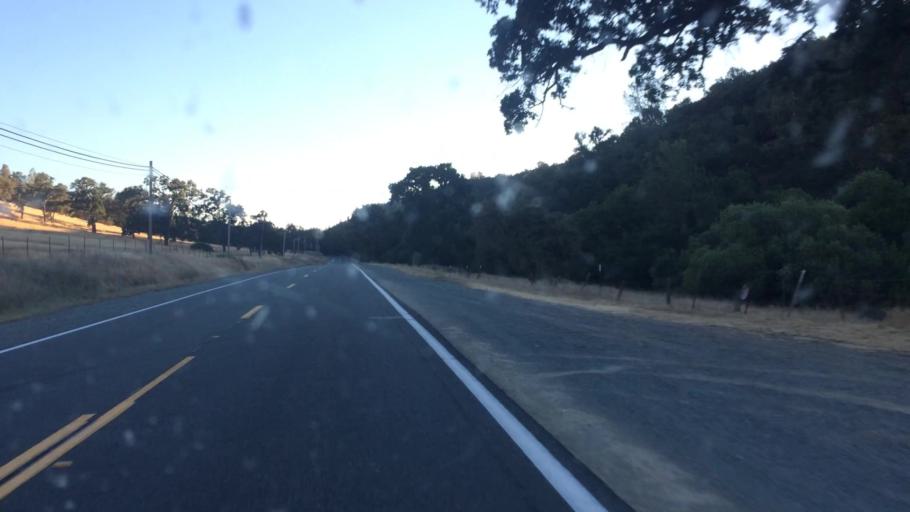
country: US
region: California
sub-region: Amador County
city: Plymouth
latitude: 38.4960
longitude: -120.8483
